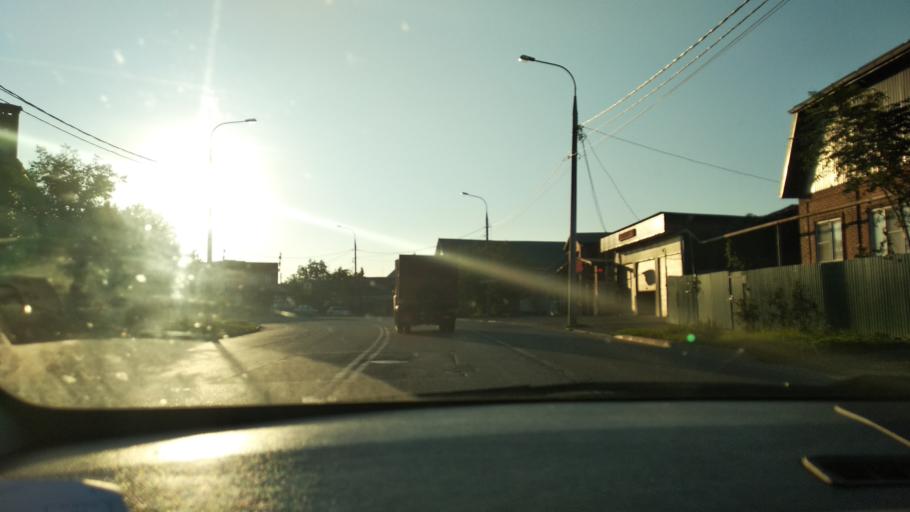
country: RU
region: Krasnodarskiy
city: Krasnodar
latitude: 45.0116
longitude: 39.0091
